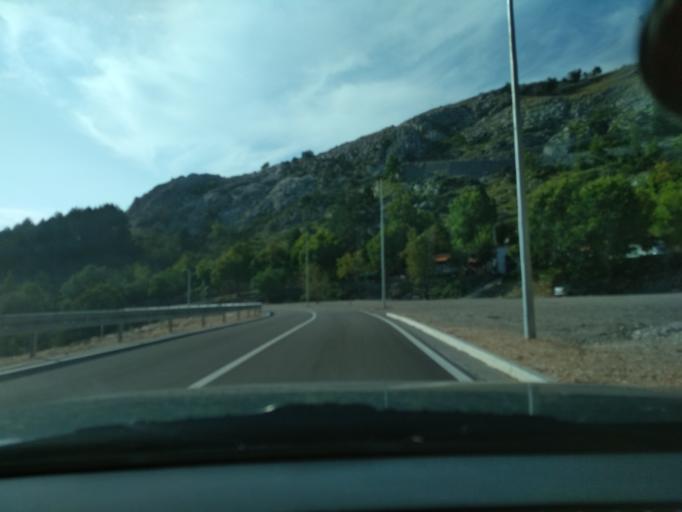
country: ME
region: Cetinje
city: Cetinje
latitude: 42.4352
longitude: 18.8478
